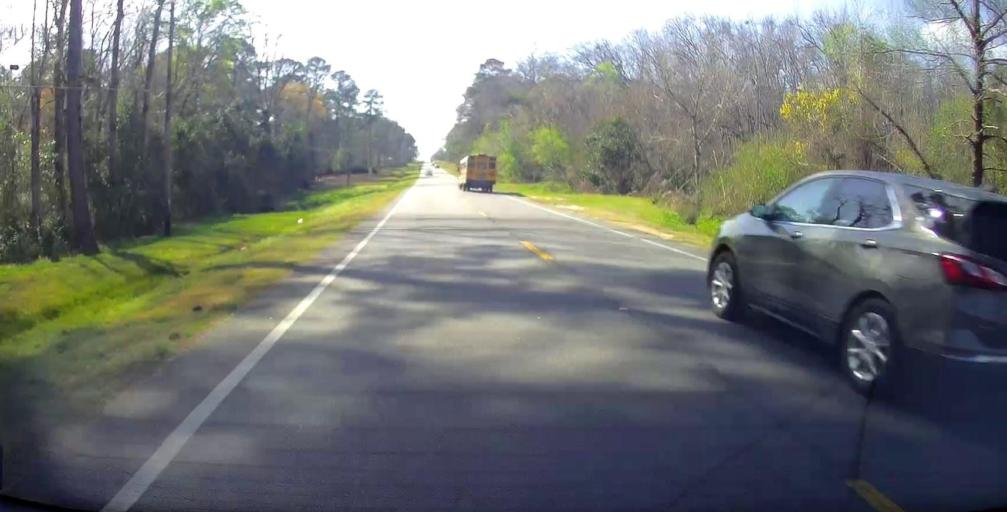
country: US
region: Georgia
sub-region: Dodge County
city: Eastman
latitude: 32.1966
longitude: -83.1954
